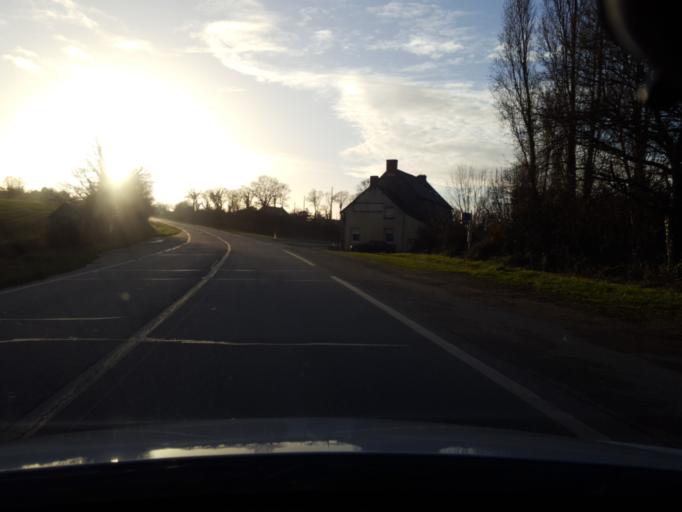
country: FR
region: Brittany
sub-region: Departement d'Ille-et-Vilaine
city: Guignen
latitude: 47.9437
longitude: -1.8327
